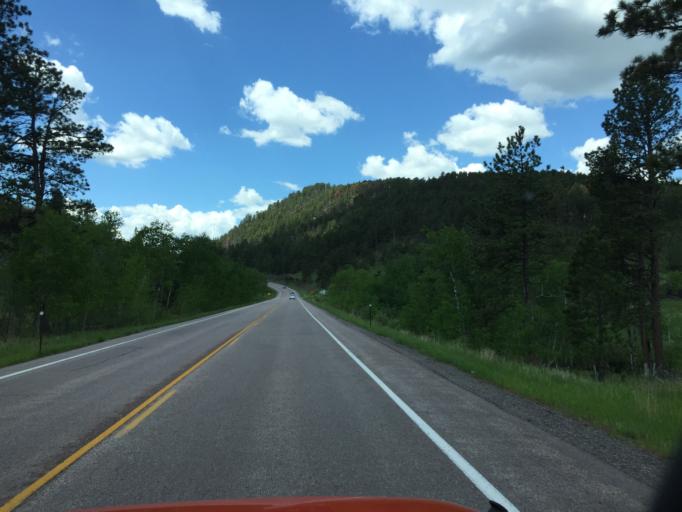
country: US
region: South Dakota
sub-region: Custer County
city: Custer
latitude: 43.8975
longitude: -103.5533
